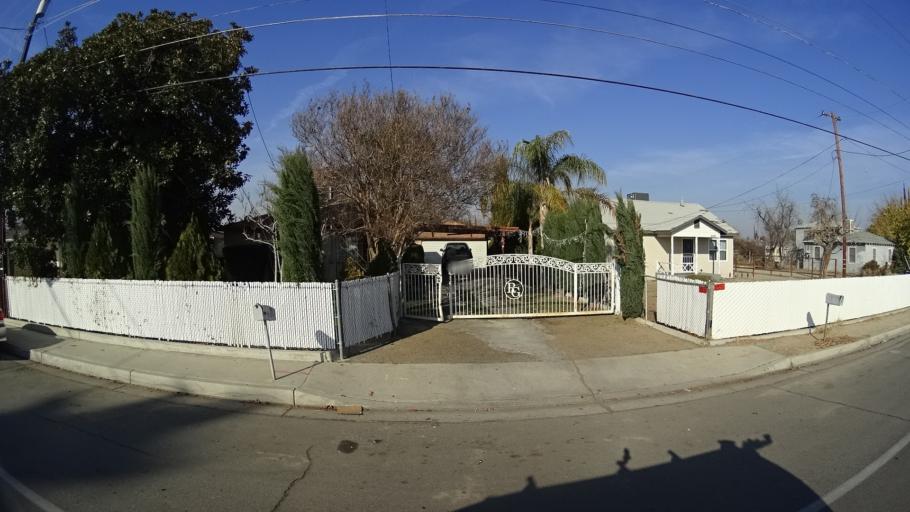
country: US
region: California
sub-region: Kern County
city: Bakersfield
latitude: 35.3251
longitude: -119.0246
